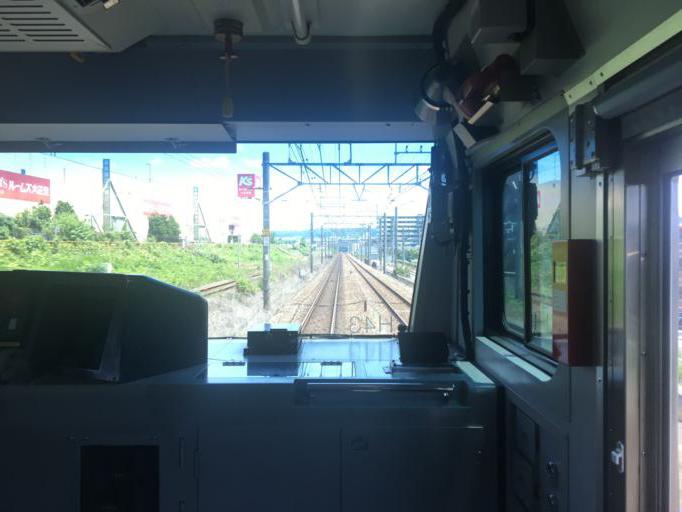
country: JP
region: Tokyo
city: Hachioji
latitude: 35.6529
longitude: 139.3501
